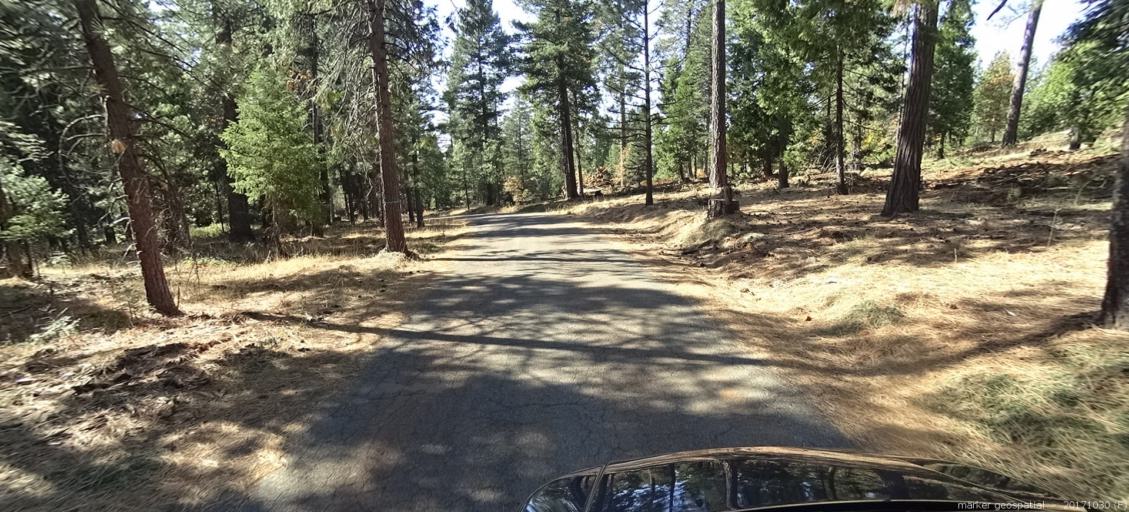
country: US
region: California
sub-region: Shasta County
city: Shingletown
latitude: 40.5153
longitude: -121.8952
